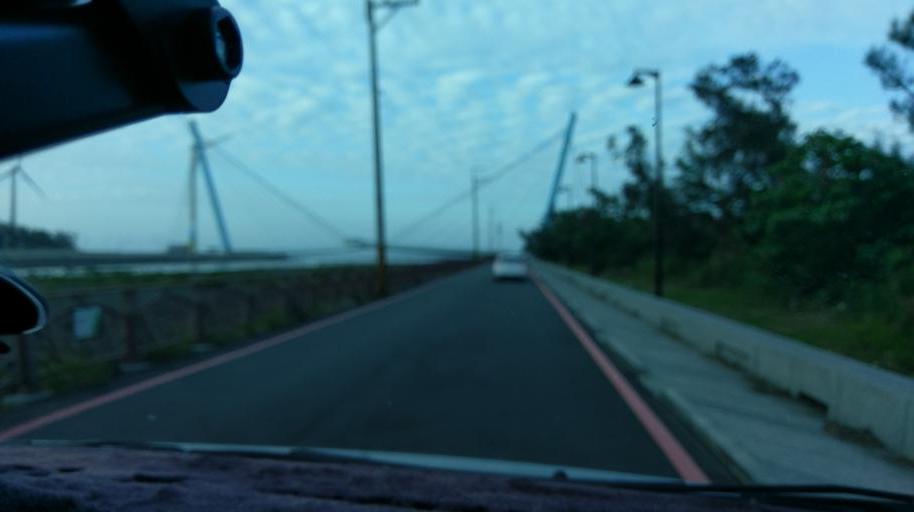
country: TW
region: Taiwan
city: Fengyuan
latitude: 24.3007
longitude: 120.5458
